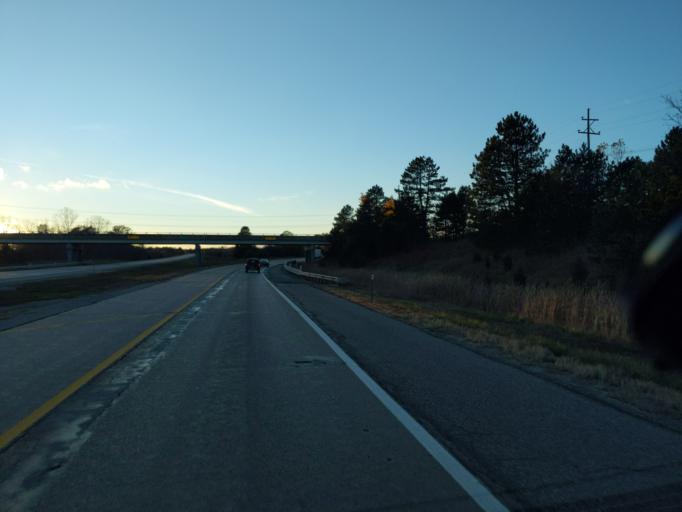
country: US
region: Michigan
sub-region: Eaton County
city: Waverly
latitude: 42.7200
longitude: -84.6603
